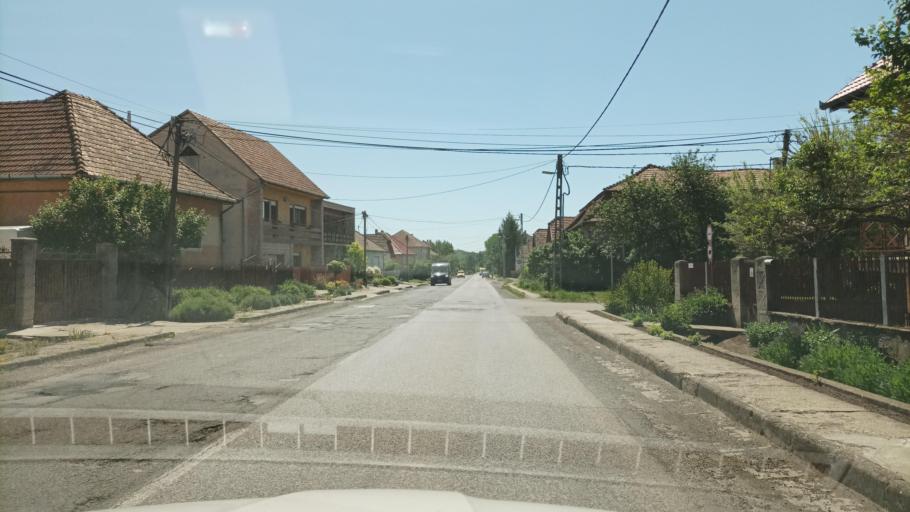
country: HU
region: Pest
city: Galgamacsa
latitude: 47.7013
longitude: 19.3966
